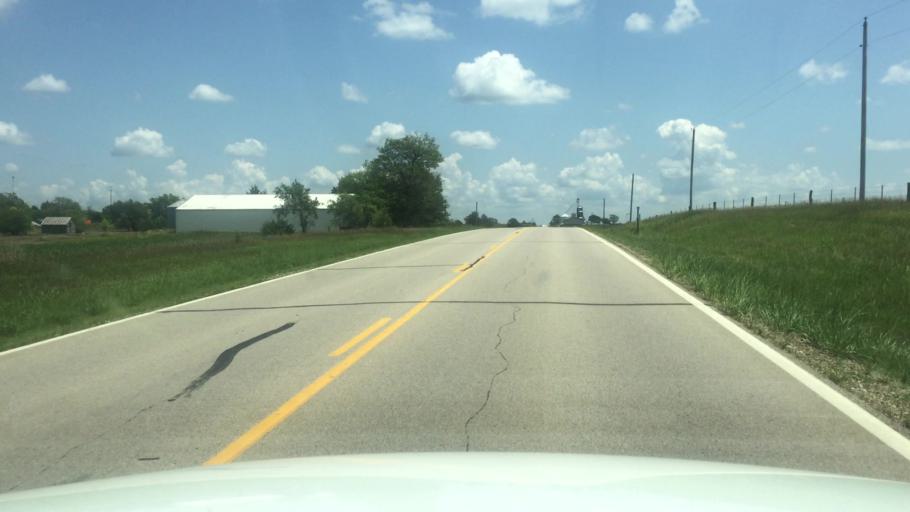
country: US
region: Kansas
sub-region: Brown County
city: Horton
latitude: 39.6673
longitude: -95.6181
